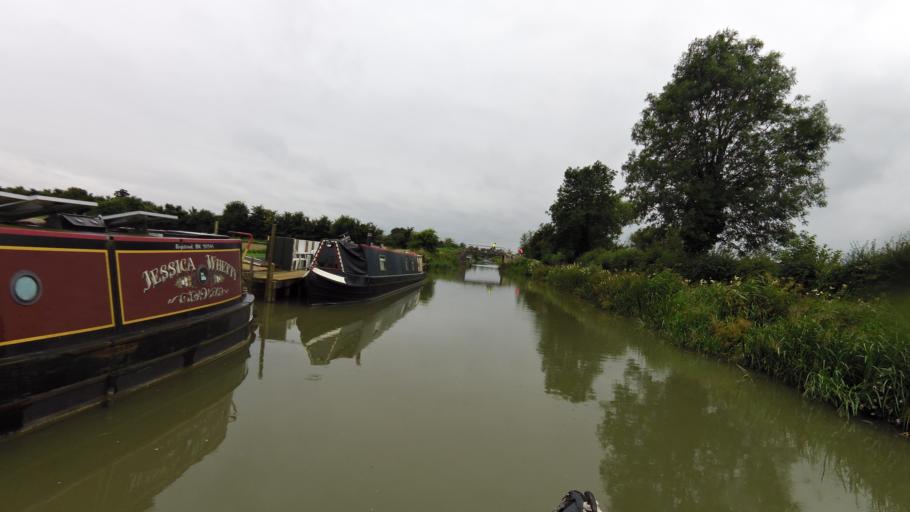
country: GB
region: England
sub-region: Wiltshire
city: Holt
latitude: 51.3436
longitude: -2.1904
